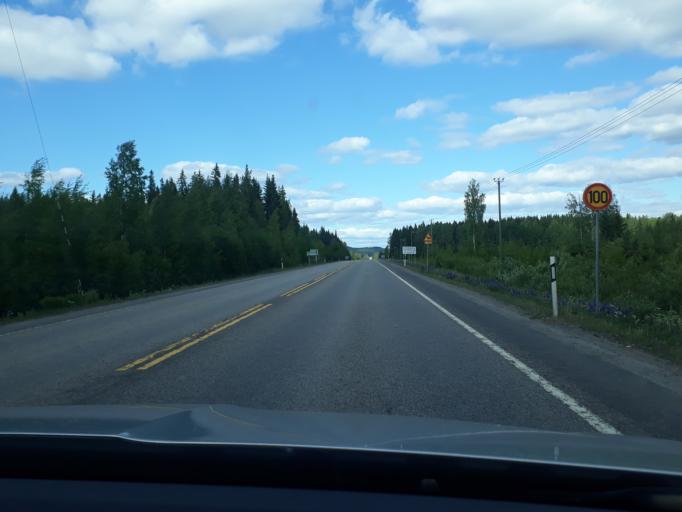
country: FI
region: Central Finland
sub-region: AEaenekoski
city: AEaenekoski
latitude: 62.6471
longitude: 25.7109
